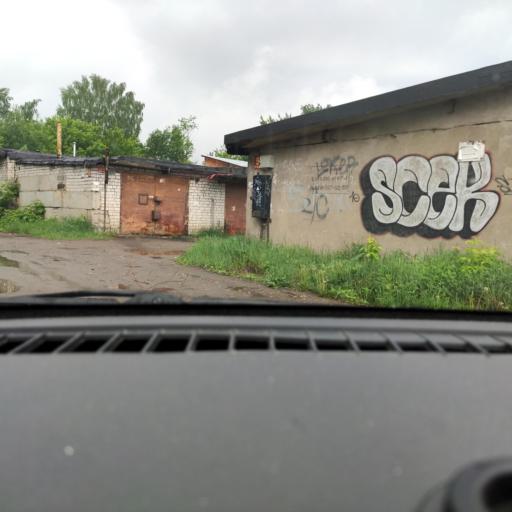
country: RU
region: Perm
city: Kultayevo
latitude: 57.9984
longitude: 55.9274
